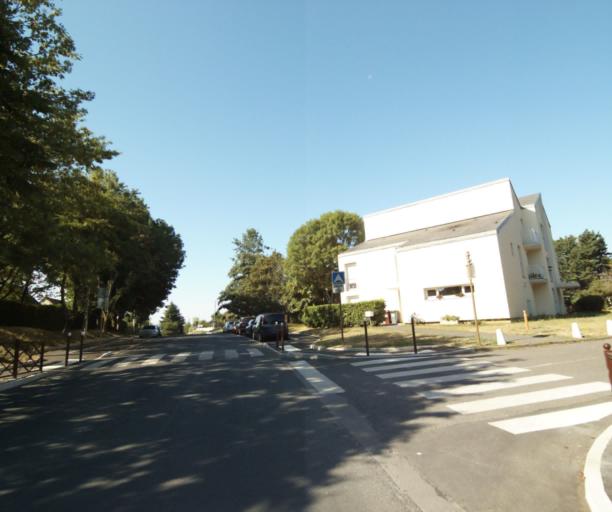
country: FR
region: Ile-de-France
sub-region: Departement de Seine-et-Marne
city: Gouvernes
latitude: 48.8669
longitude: 2.6989
